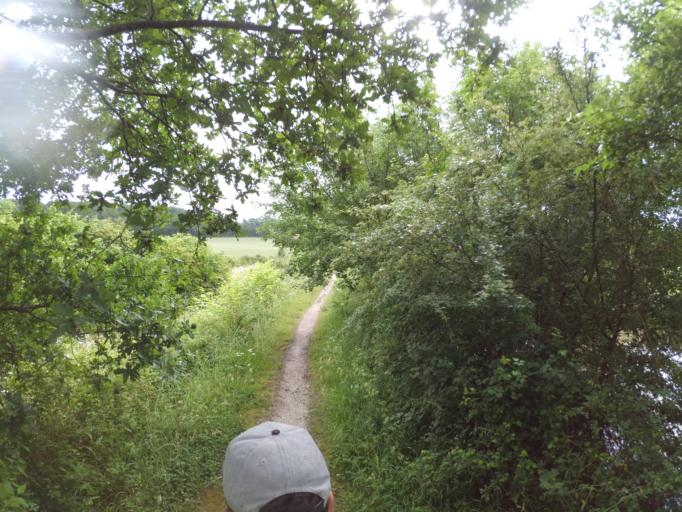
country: FR
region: Pays de la Loire
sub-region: Departement de la Vendee
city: Nesmy
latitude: 46.6183
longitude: -1.4097
